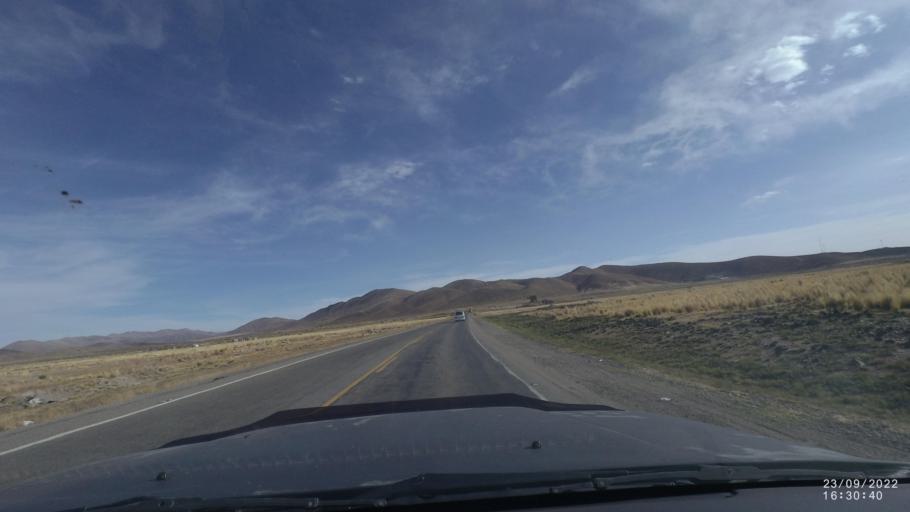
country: BO
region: Oruro
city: Machacamarca
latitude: -18.1571
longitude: -66.9863
